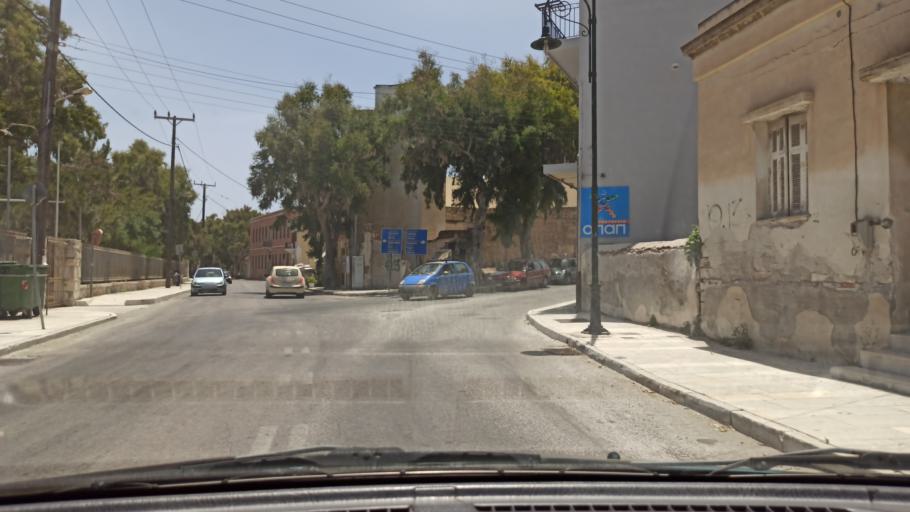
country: GR
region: South Aegean
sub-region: Nomos Kykladon
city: Ermoupolis
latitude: 37.4321
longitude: 24.9350
